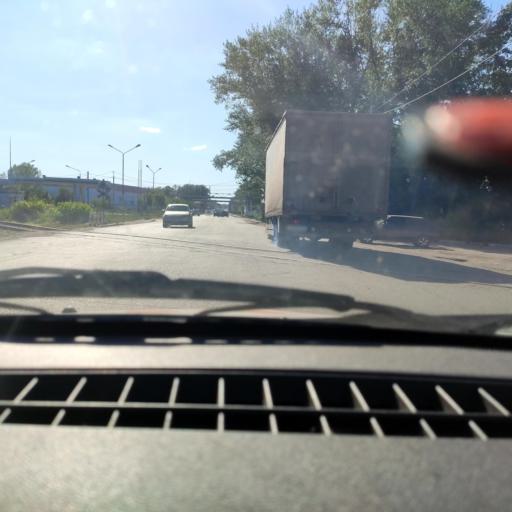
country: RU
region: Bashkortostan
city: Sterlitamak
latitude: 53.6530
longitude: 55.9704
